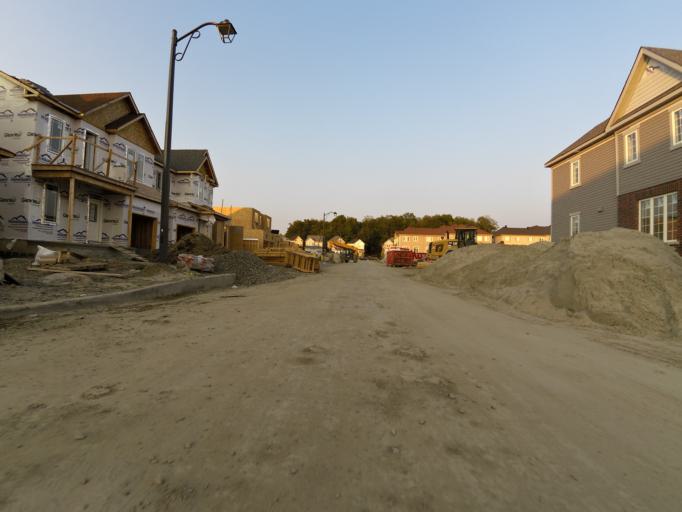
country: CA
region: Ontario
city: Bells Corners
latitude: 45.2778
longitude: -75.8443
